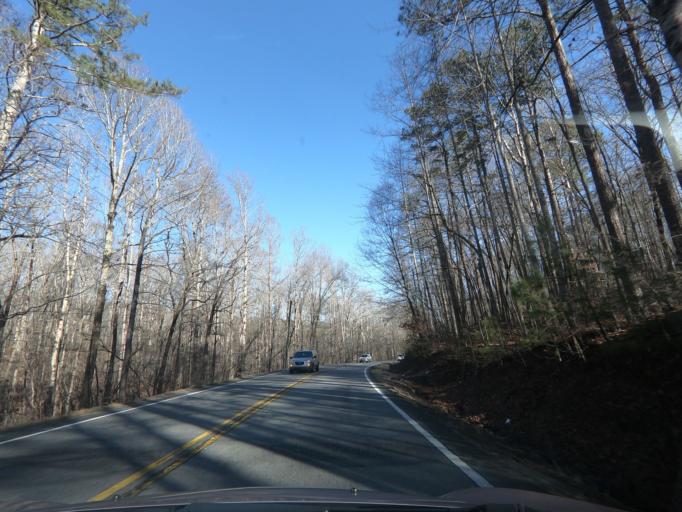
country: US
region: Georgia
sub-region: Dawson County
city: Dawsonville
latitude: 34.3458
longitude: -84.1160
